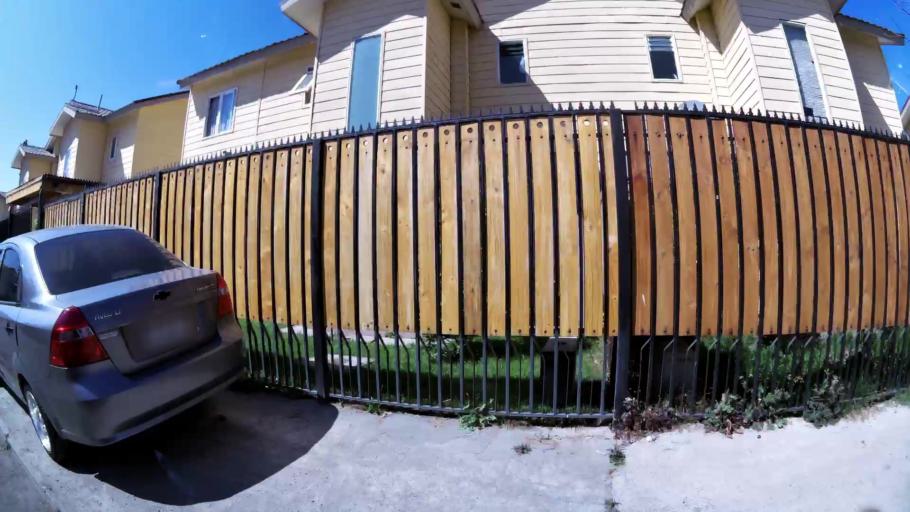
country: CL
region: Santiago Metropolitan
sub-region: Provincia de Chacabuco
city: Chicureo Abajo
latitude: -33.3302
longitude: -70.7516
